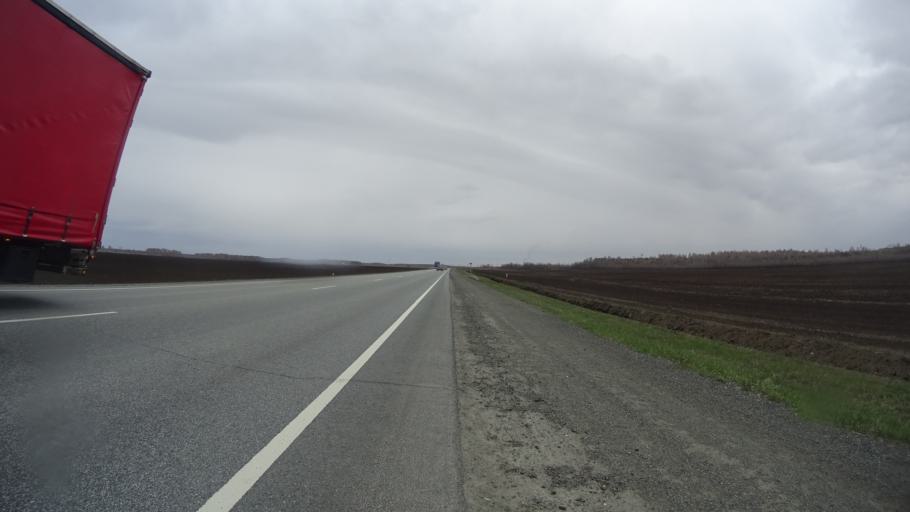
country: RU
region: Chelyabinsk
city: Krasnogorskiy
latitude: 54.5726
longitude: 61.2908
